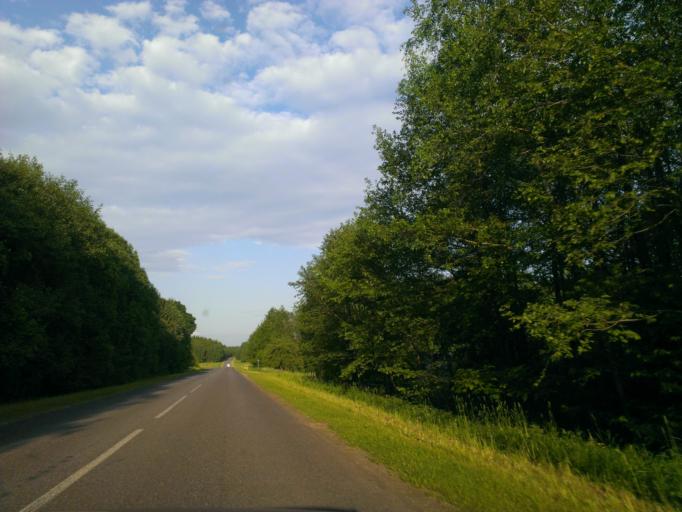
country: LT
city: Plateliai
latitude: 56.0636
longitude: 21.8990
